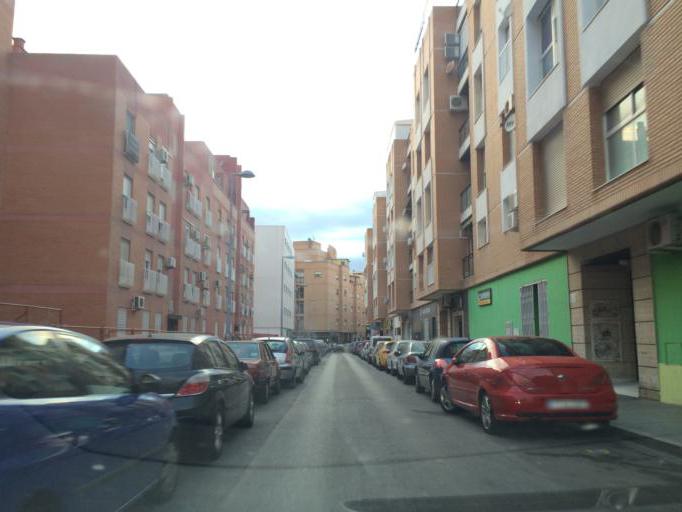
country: ES
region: Andalusia
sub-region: Provincia de Almeria
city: Almeria
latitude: 36.8344
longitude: -2.4500
